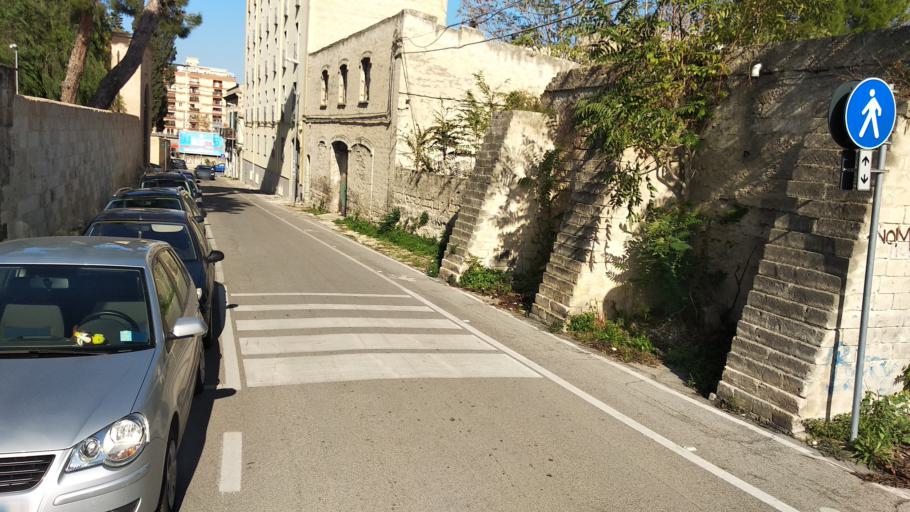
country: IT
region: Apulia
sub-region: Provincia di Bari
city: Bari
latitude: 41.1153
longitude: 16.8576
